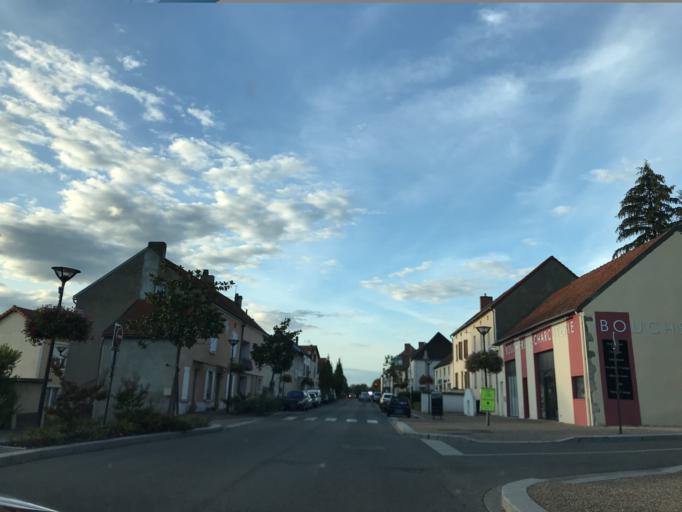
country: FR
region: Auvergne
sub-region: Departement de l'Allier
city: Abrest
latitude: 46.0966
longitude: 3.4465
